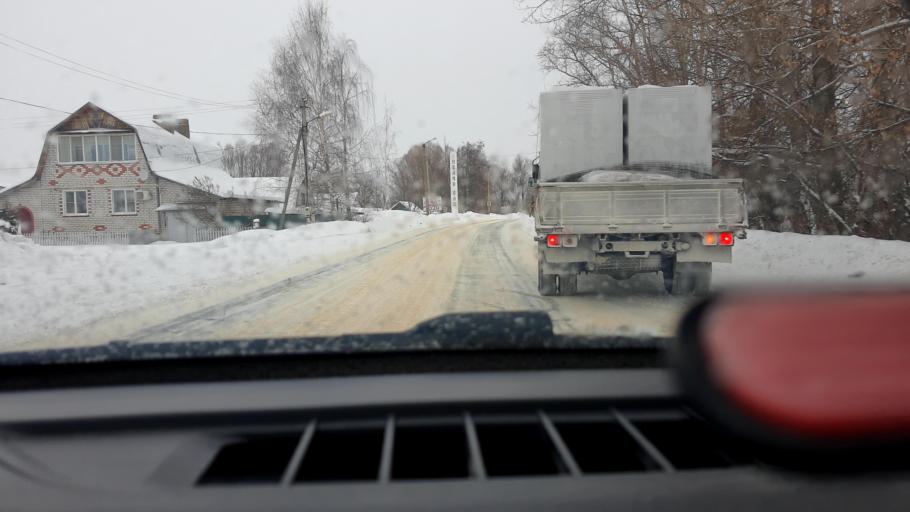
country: RU
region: Nizjnij Novgorod
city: Buturlino
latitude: 55.5691
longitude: 44.9062
